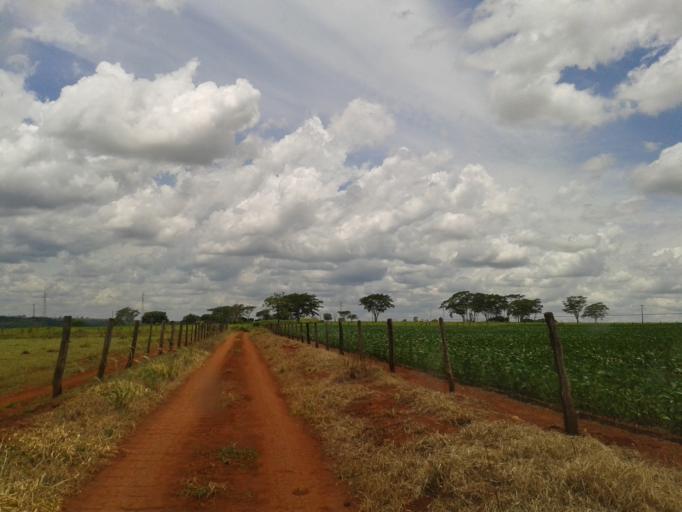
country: BR
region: Minas Gerais
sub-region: Centralina
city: Centralina
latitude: -18.7119
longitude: -49.2160
